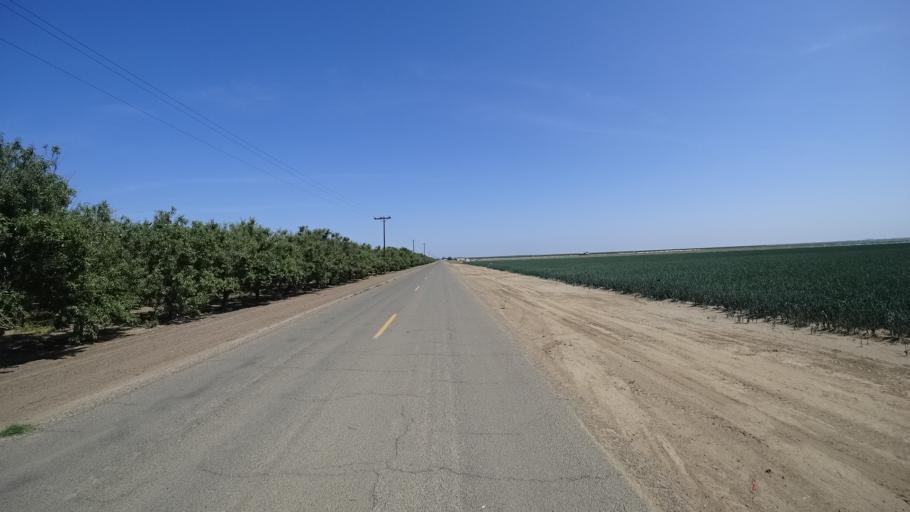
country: US
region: California
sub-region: Kings County
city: Kettleman City
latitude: 36.0666
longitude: -120.0037
